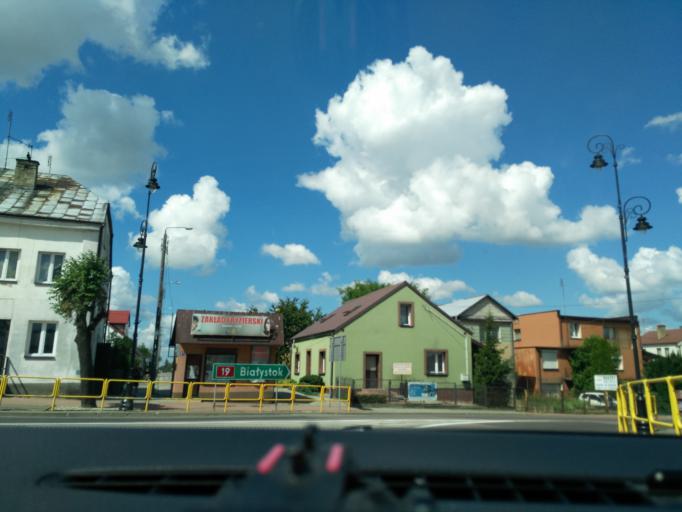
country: PL
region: Podlasie
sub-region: Powiat siemiatycki
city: Siemiatycze
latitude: 52.4286
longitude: 22.8622
